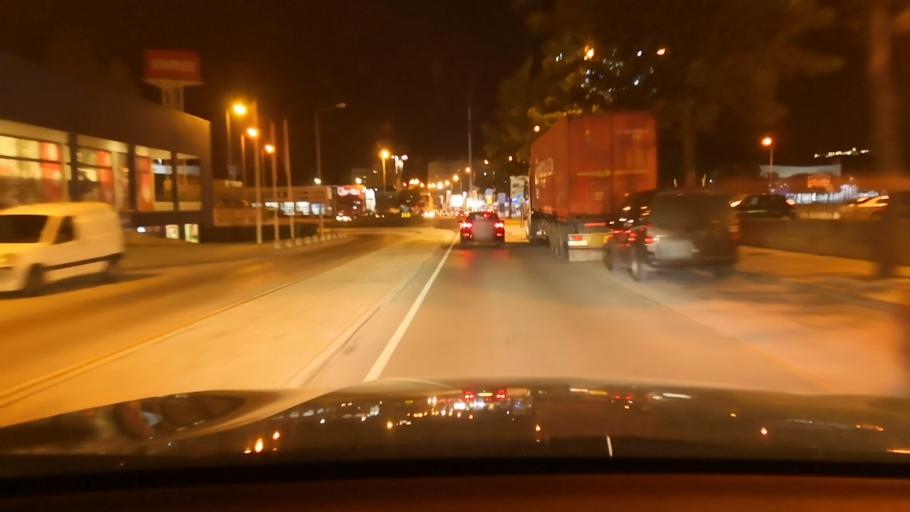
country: PT
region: Setubal
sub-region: Setubal
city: Setubal
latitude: 38.5398
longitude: -8.8682
